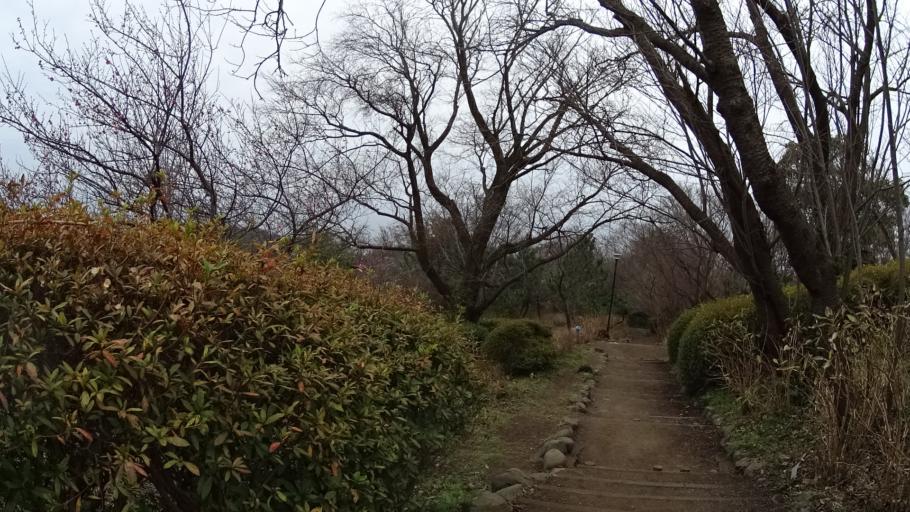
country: JP
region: Kanagawa
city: Oiso
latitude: 35.3195
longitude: 139.3090
